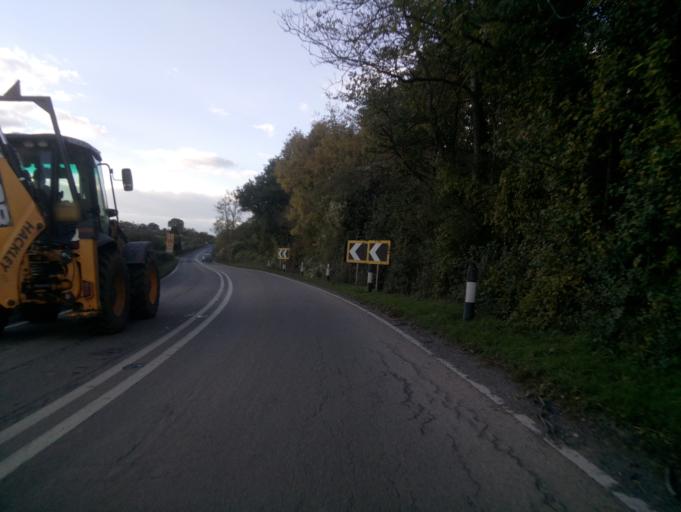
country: GB
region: England
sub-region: Herefordshire
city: Ledbury
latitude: 52.0484
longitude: -2.4445
